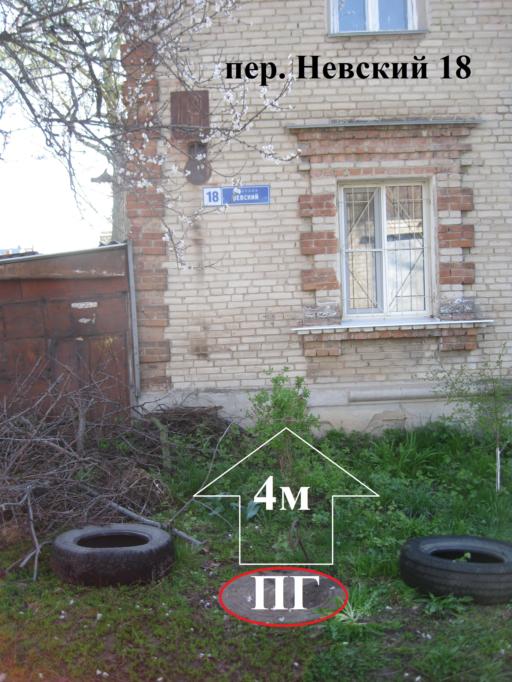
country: RU
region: Voronezj
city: Voronezh
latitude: 51.6430
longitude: 39.2041
